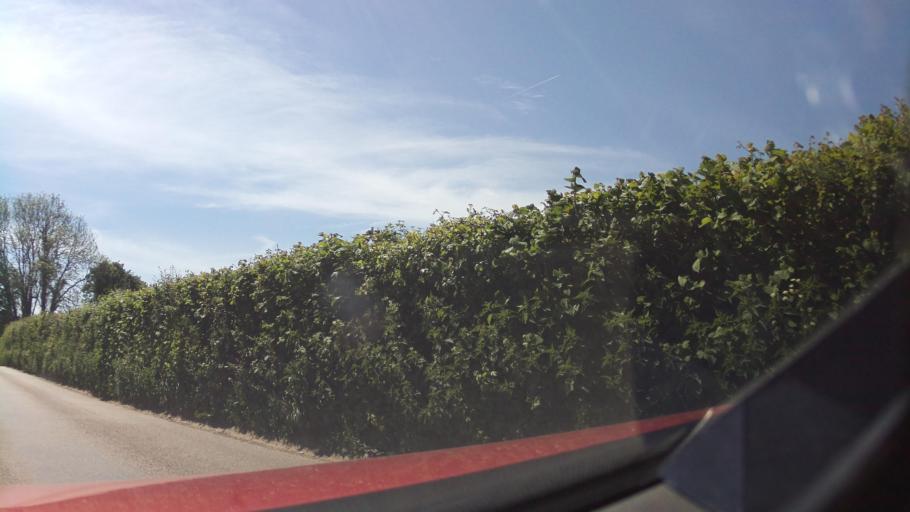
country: GB
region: England
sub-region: Devon
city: Ottery St Mary
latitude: 50.7451
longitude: -3.2760
